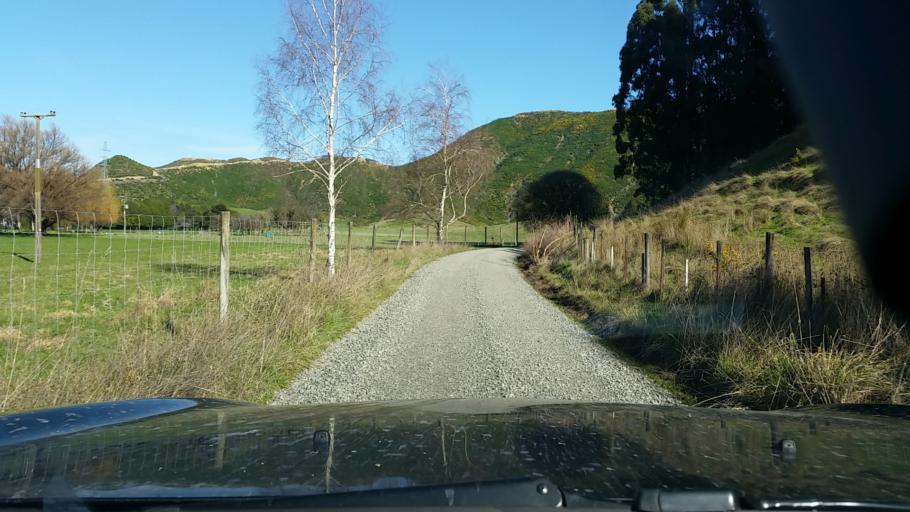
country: NZ
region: Marlborough
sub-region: Marlborough District
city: Blenheim
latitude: -41.4627
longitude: 173.7969
